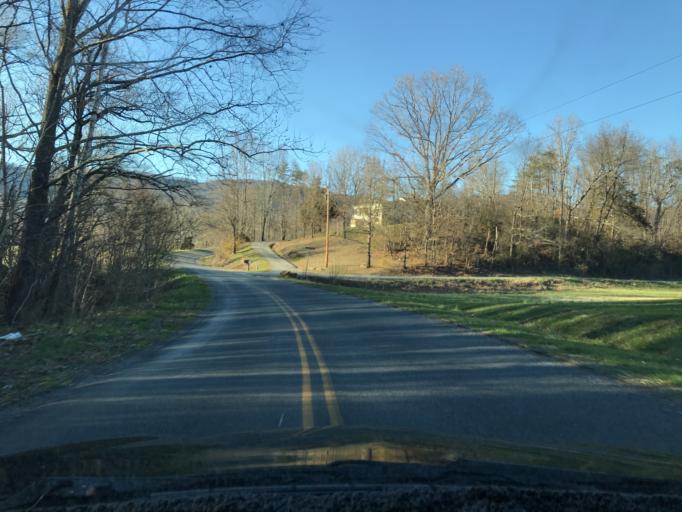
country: US
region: Virginia
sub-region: Botetourt County
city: Buchanan
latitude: 37.4502
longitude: -79.6653
